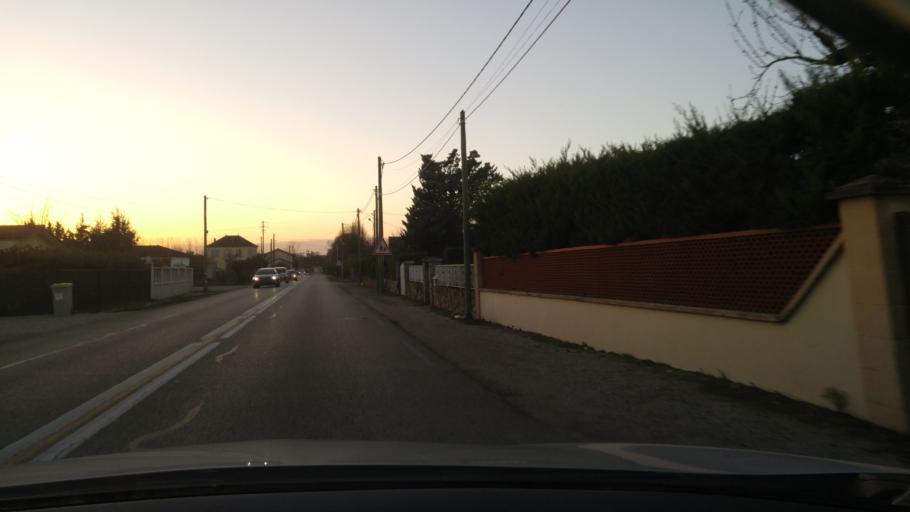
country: FR
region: Rhone-Alpes
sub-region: Departement de l'Isere
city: Tignieu-Jameyzieu
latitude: 45.7161
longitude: 5.1667
